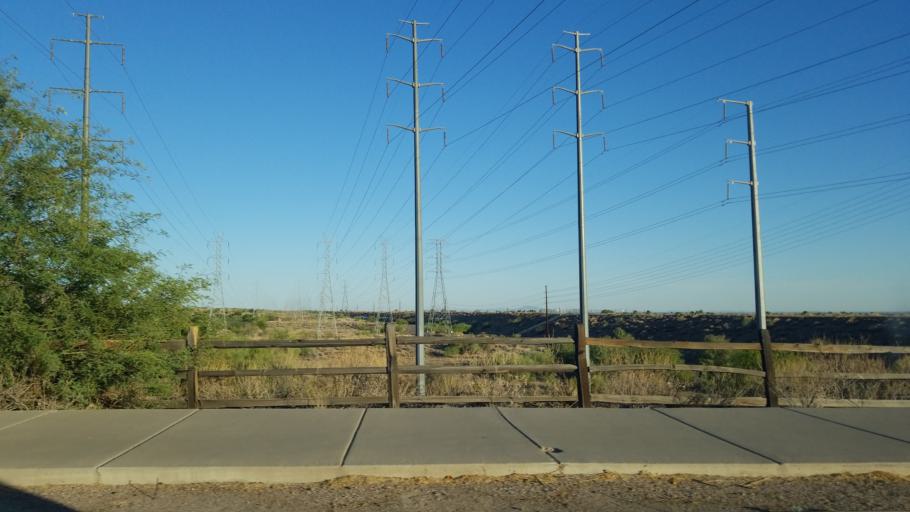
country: US
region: Arizona
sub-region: Maricopa County
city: Paradise Valley
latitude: 33.6256
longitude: -111.8682
